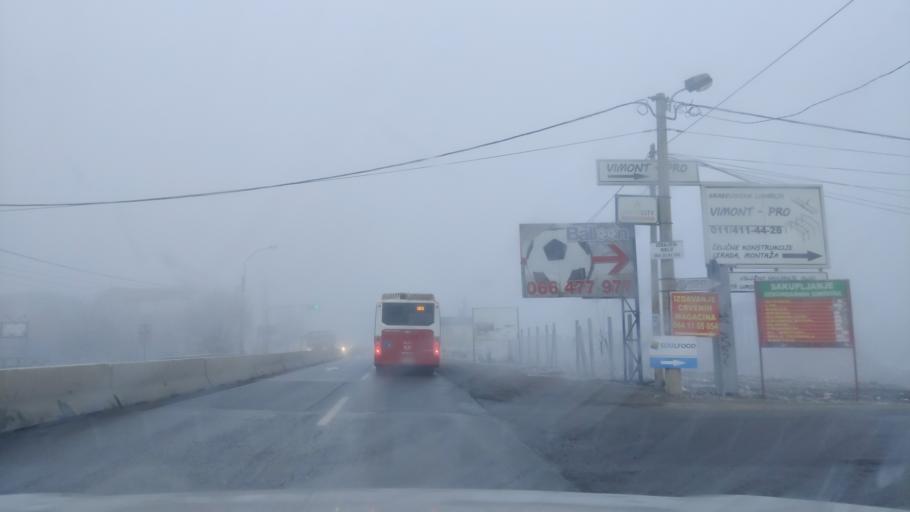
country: RS
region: Central Serbia
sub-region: Belgrade
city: Stari Grad
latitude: 44.8524
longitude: 20.4844
